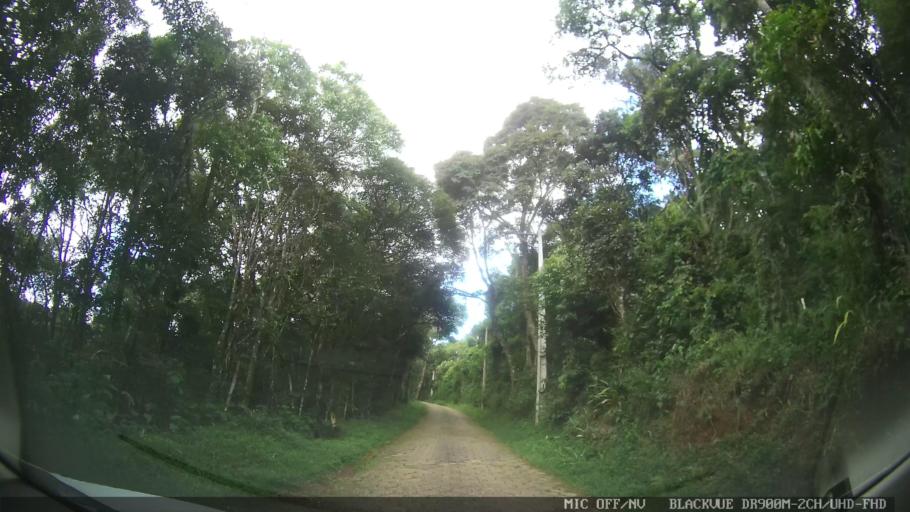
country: BR
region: Minas Gerais
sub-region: Extrema
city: Extrema
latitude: -22.8823
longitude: -46.3139
